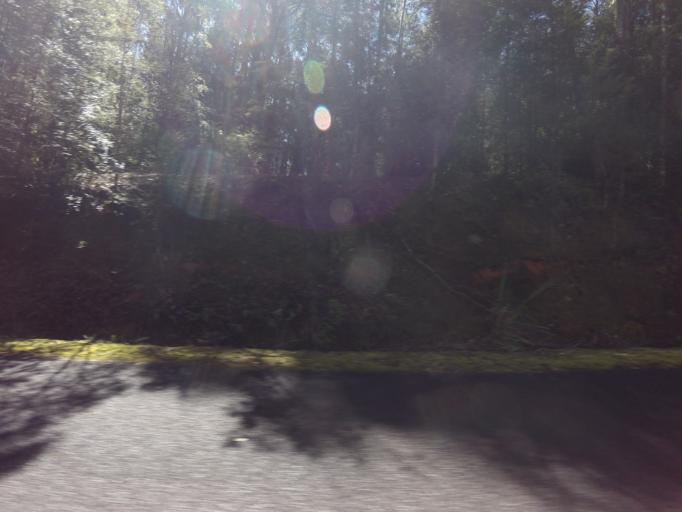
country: AU
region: Tasmania
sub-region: Huon Valley
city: Geeveston
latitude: -42.8243
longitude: 146.3149
